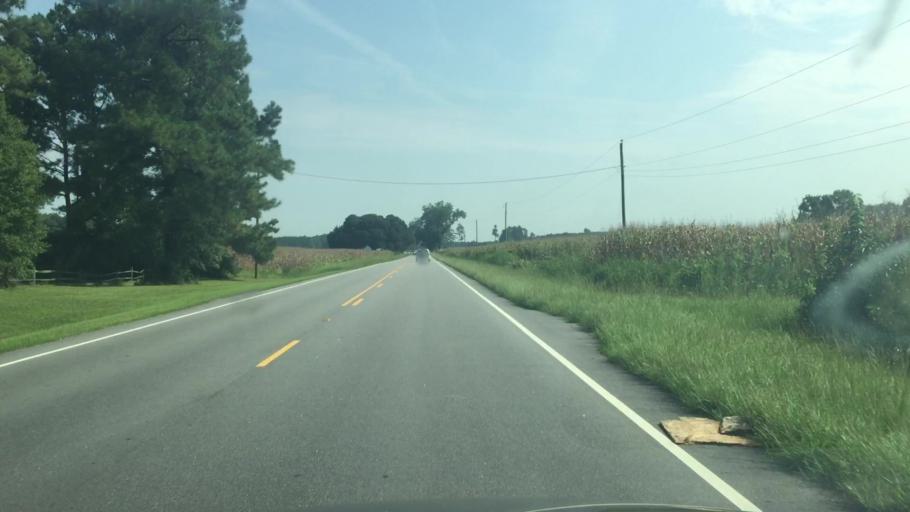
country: US
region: North Carolina
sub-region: Columbus County
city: Tabor City
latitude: 34.1660
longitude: -78.8445
